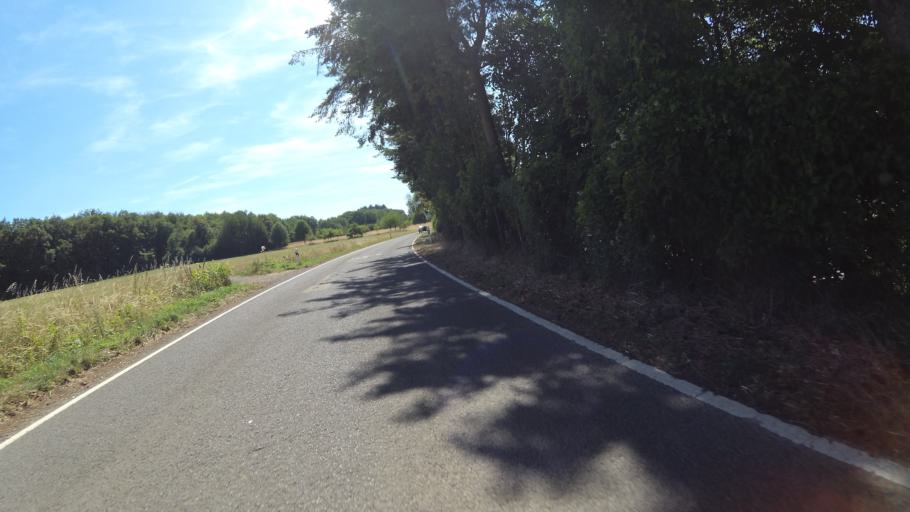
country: DE
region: Rheinland-Pfalz
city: Zweibrucken
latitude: 49.2330
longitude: 7.3200
